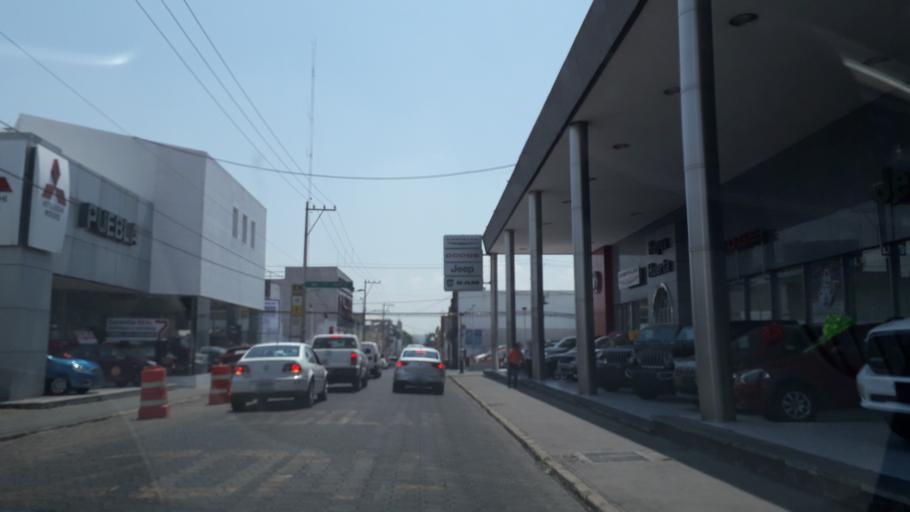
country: MX
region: Puebla
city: Puebla
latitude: 19.0506
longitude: -98.2108
